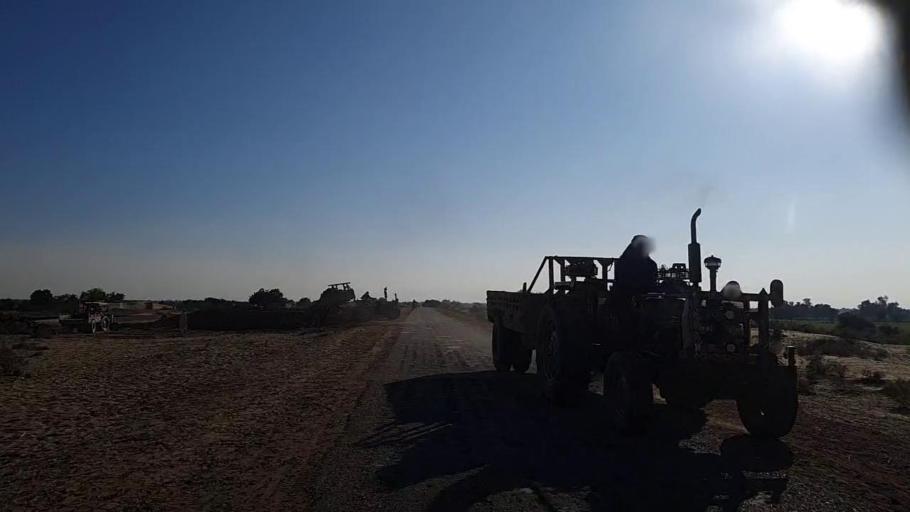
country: PK
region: Sindh
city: Khairpur
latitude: 27.9017
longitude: 69.7487
